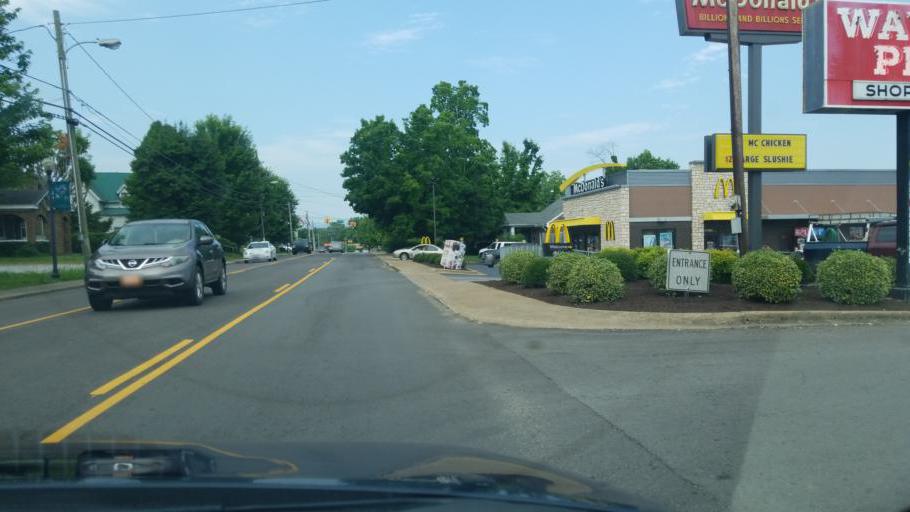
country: US
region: Tennessee
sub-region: Humphreys County
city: Waverly
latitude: 36.0838
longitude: -87.7996
